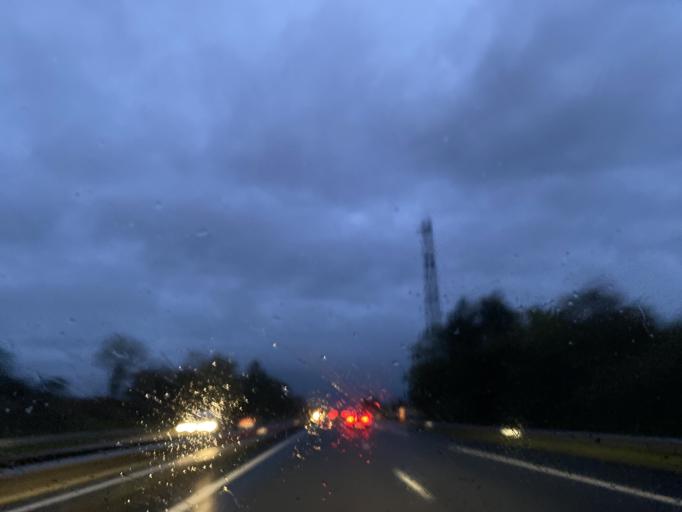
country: FR
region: Auvergne
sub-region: Departement de l'Allier
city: Doyet
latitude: 46.3428
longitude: 2.8763
